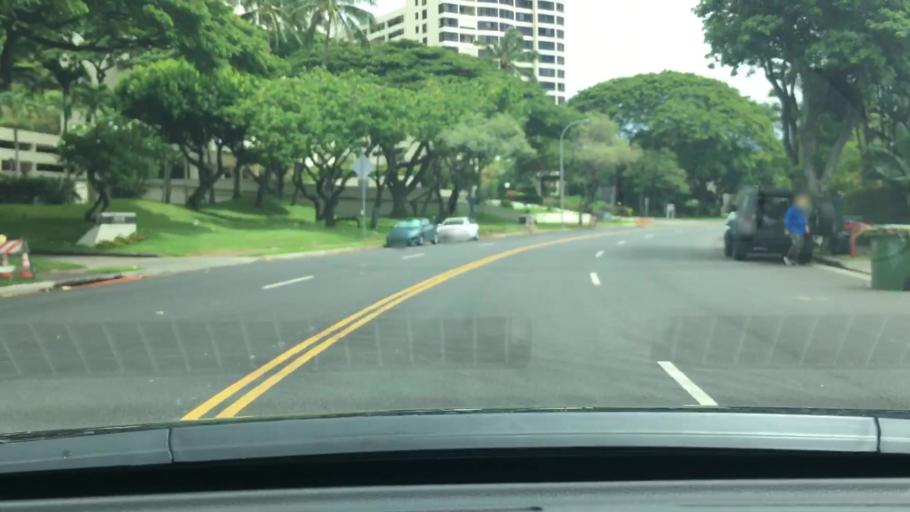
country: US
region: Hawaii
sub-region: Honolulu County
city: Waimanalo Beach
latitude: 21.2932
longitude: -157.7078
